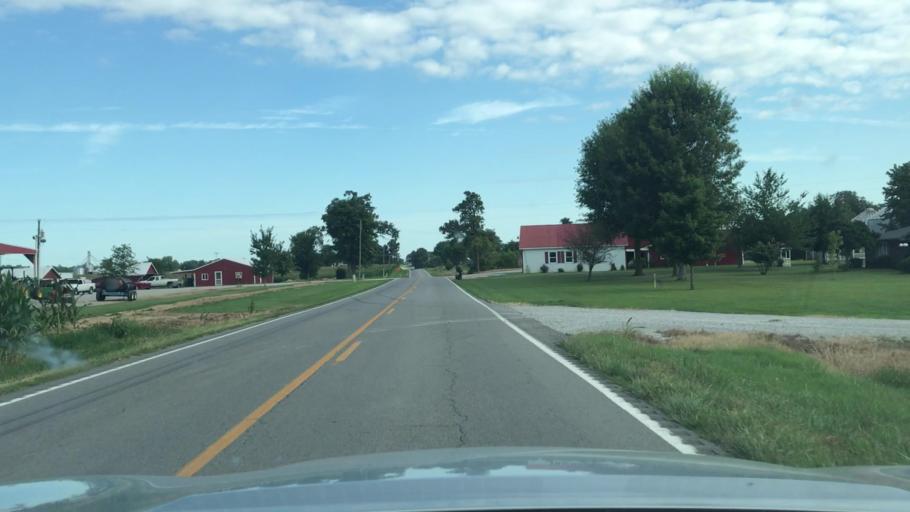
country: US
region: Kentucky
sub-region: Todd County
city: Elkton
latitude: 36.8587
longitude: -87.1592
